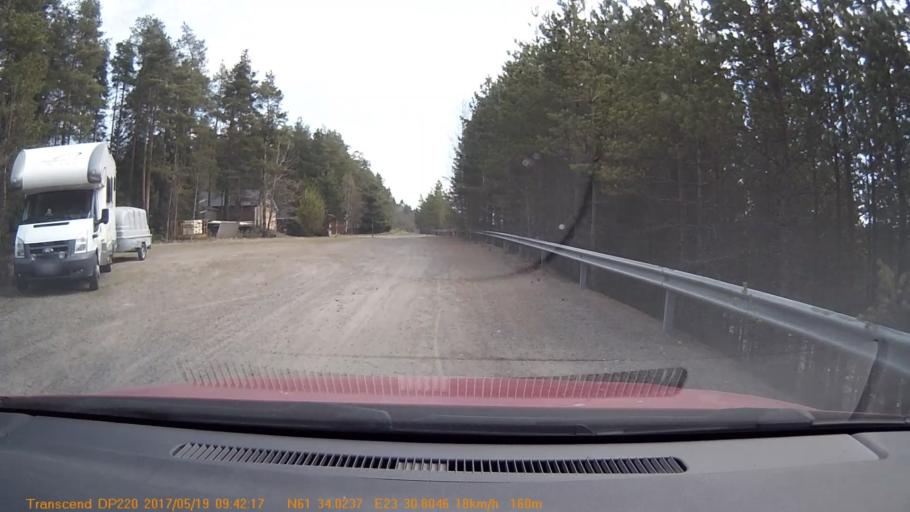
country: FI
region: Pirkanmaa
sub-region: Tampere
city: Yloejaervi
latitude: 61.5671
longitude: 23.5132
